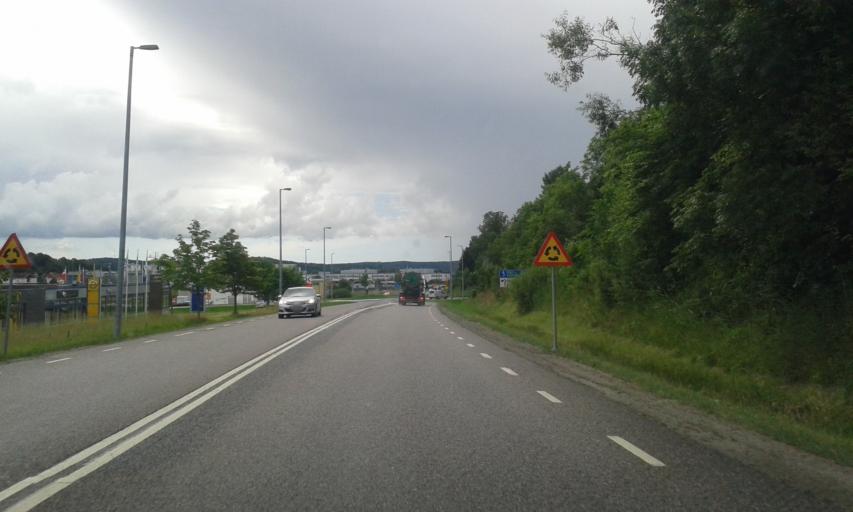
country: SE
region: Vaestra Goetaland
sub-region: Kungalvs Kommun
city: Kungalv
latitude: 57.8833
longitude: 11.9820
